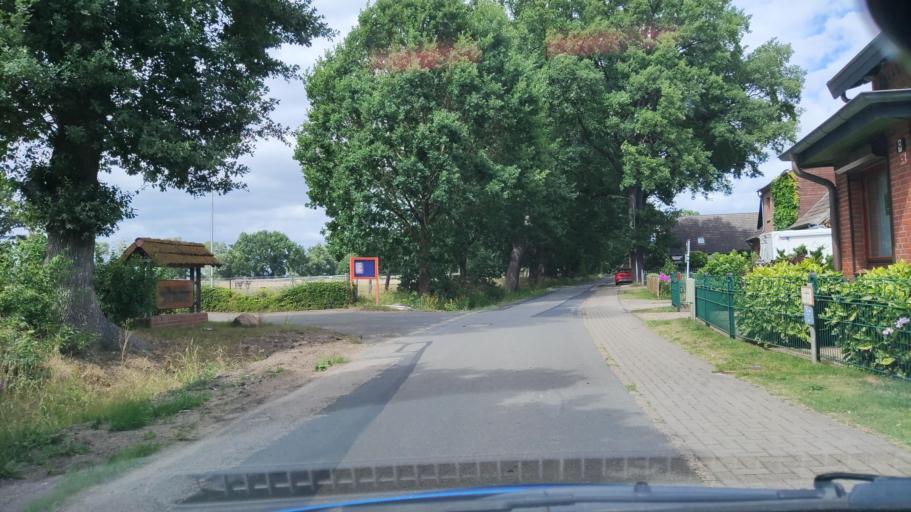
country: DE
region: Lower Saxony
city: Stelle
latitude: 53.4124
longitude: 10.0657
